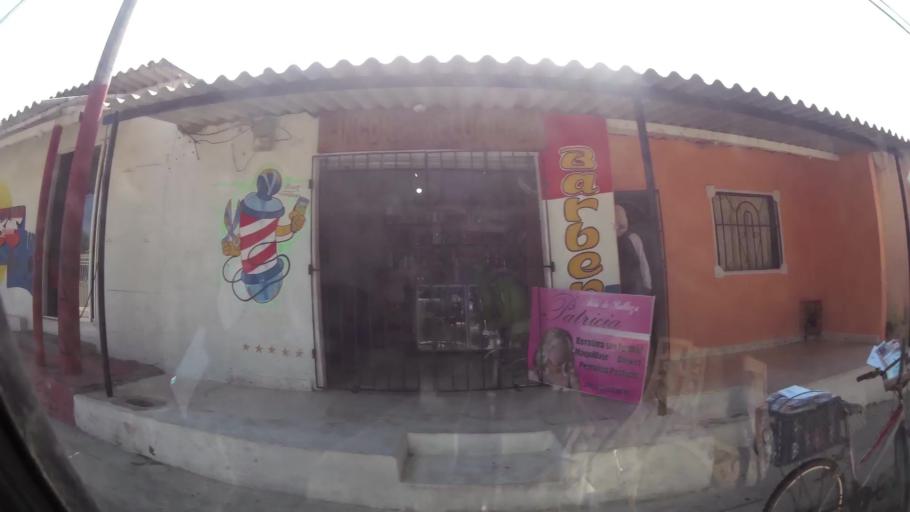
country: CO
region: Atlantico
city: Barranquilla
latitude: 10.9788
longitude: -74.8248
